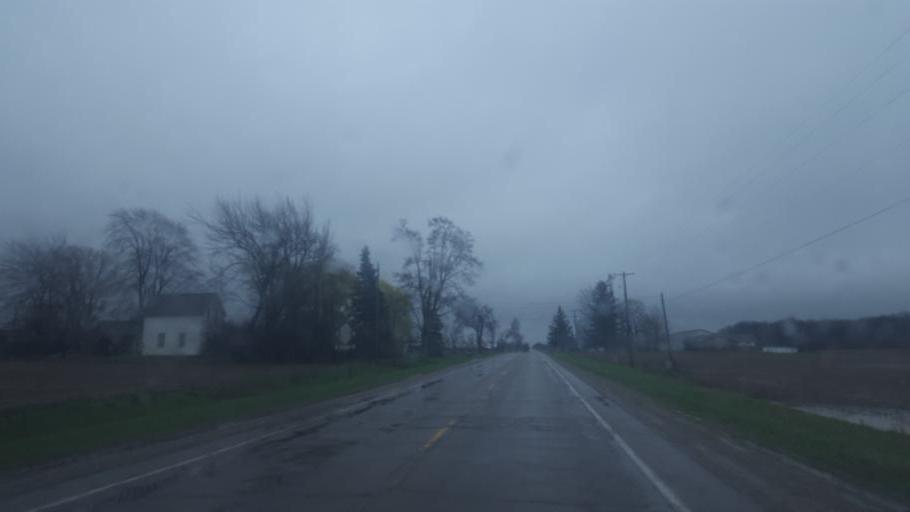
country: US
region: Michigan
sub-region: Isabella County
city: Mount Pleasant
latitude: 43.6532
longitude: -84.7682
